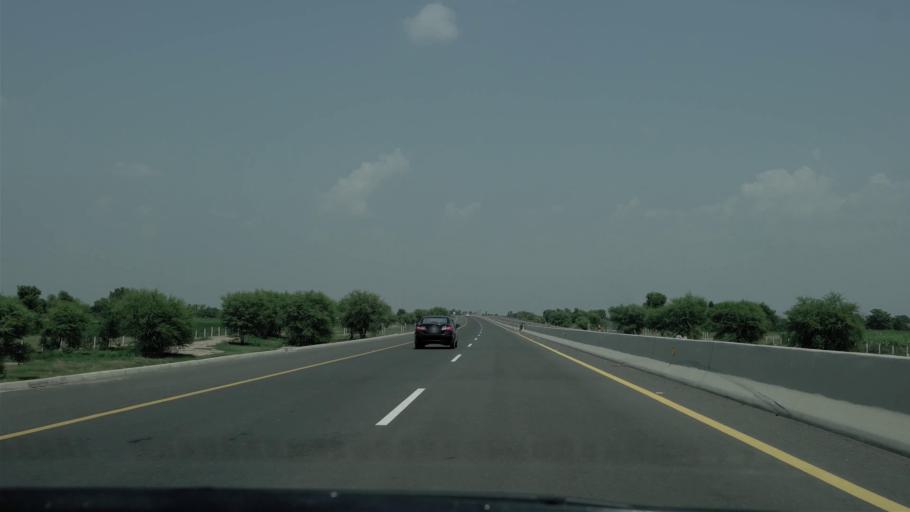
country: PK
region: Punjab
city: Gojra
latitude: 31.1894
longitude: 72.6478
